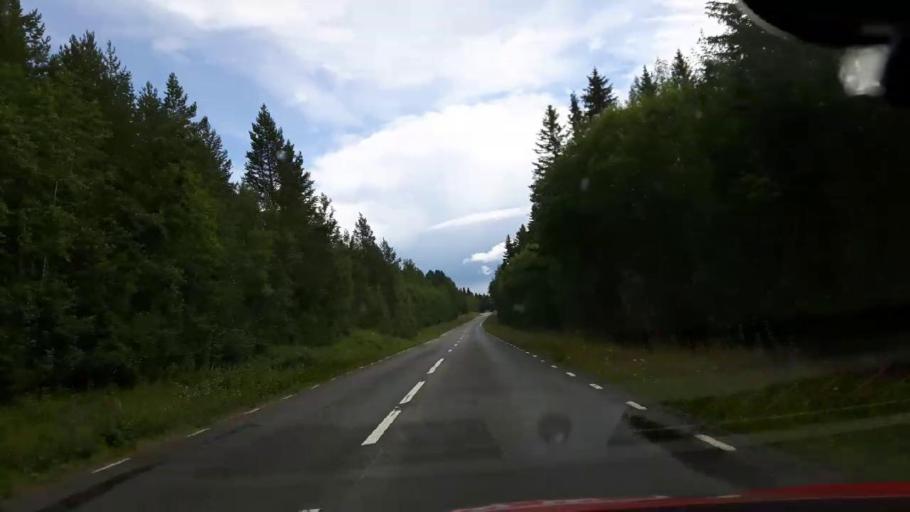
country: SE
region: Jaemtland
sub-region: Stroemsunds Kommun
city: Stroemsund
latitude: 64.3416
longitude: 14.9478
